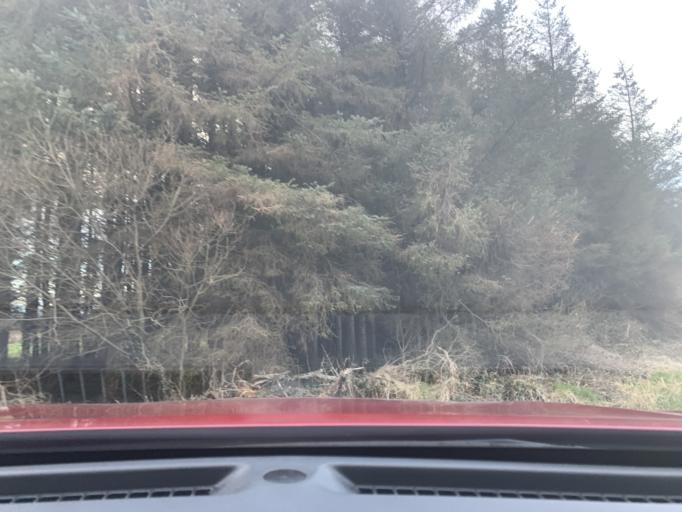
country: IE
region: Connaught
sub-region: Roscommon
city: Ballaghaderreen
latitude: 53.8893
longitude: -8.5818
